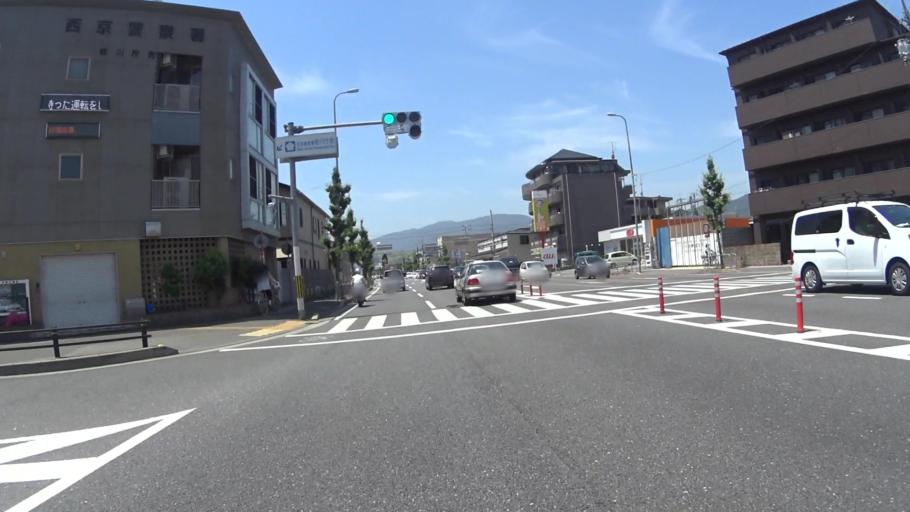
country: JP
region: Kyoto
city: Muko
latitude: 34.9910
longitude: 135.7031
